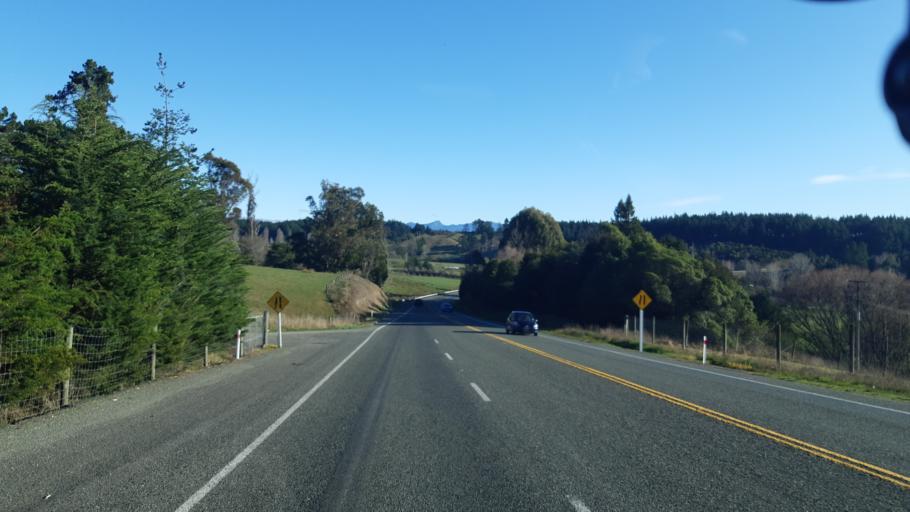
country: NZ
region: Tasman
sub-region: Tasman District
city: Mapua
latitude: -41.2830
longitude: 173.0750
